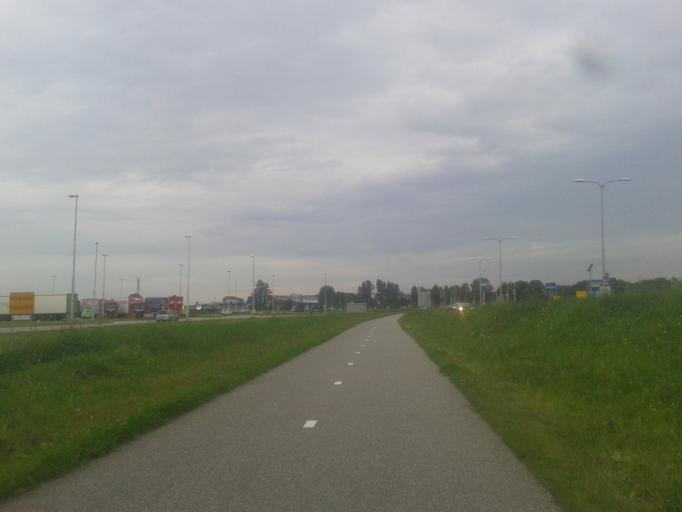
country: NL
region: South Holland
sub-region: Gemeente Leiderdorp
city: Leiderdorp
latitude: 52.1636
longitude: 4.5551
